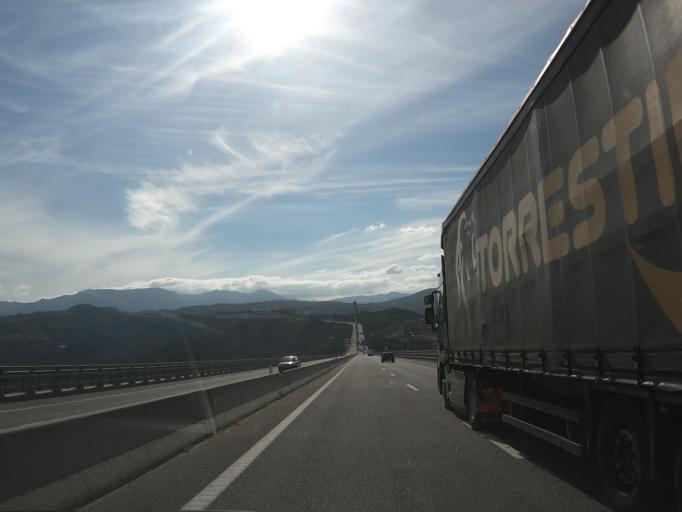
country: PT
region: Vila Real
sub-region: Vila Real
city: Vila Real
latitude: 41.2748
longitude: -7.7410
